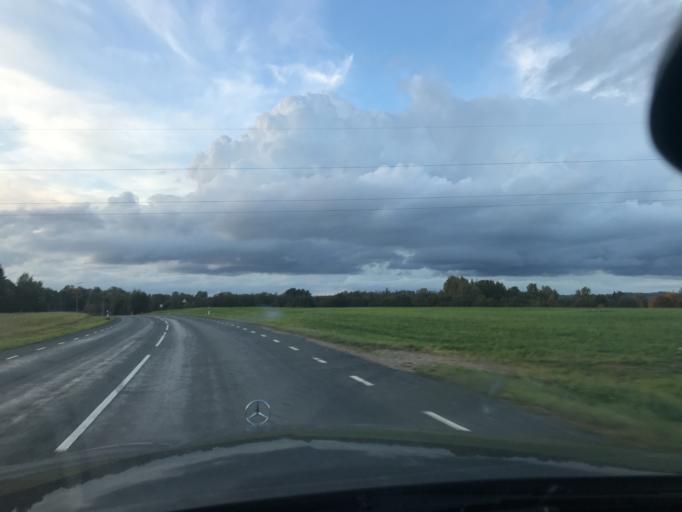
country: EE
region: Vorumaa
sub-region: Antsla vald
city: Vana-Antsla
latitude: 57.9241
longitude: 26.3414
